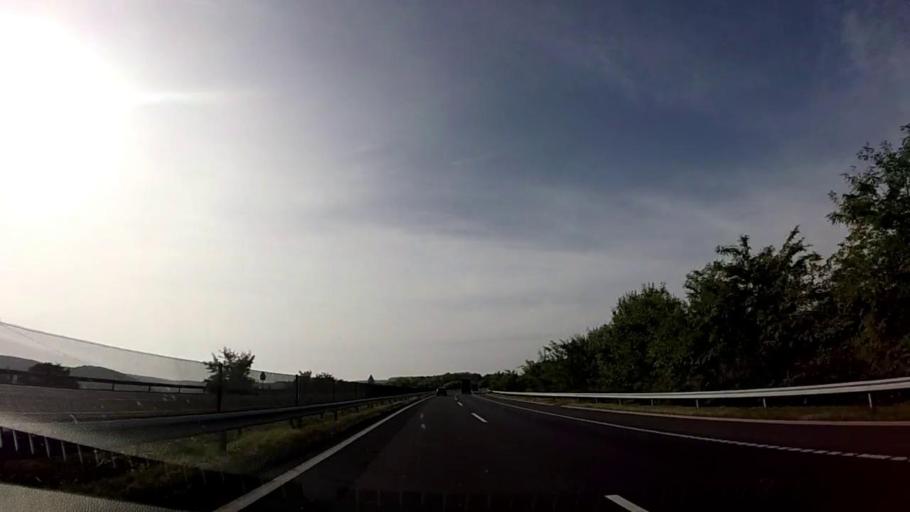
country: HU
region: Somogy
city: Zamardi
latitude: 46.8379
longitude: 17.9510
